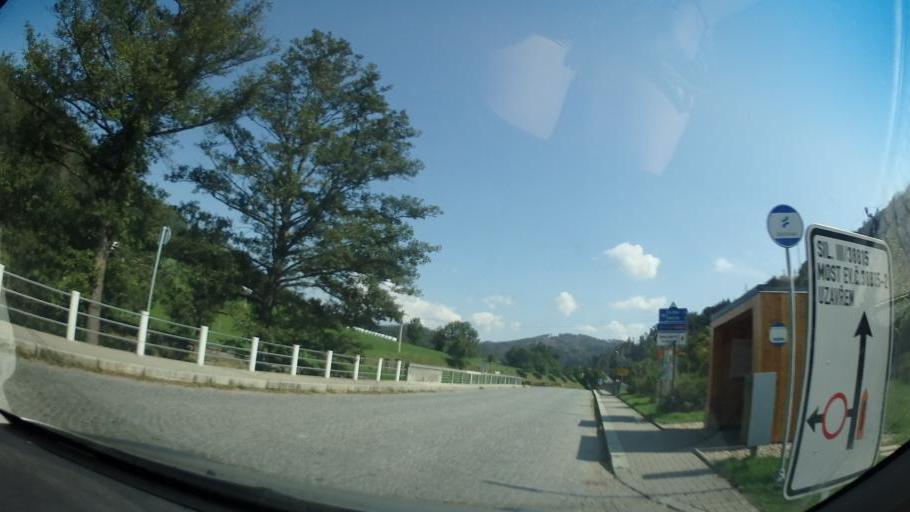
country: CZ
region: Vysocina
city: Bystrice nad Pernstejnem
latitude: 49.5568
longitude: 16.3151
